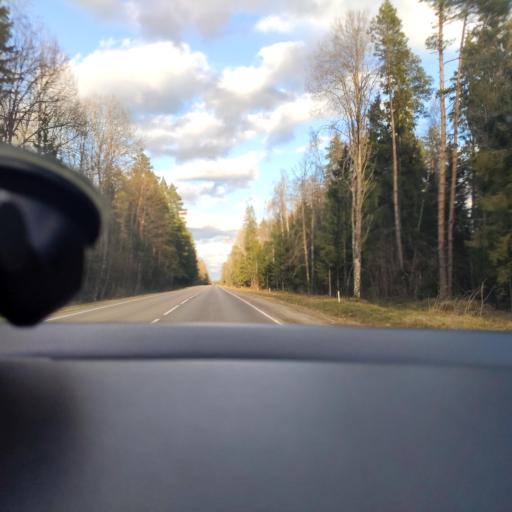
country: RU
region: Moskovskaya
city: Shaturtorf
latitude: 55.4303
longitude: 39.3646
